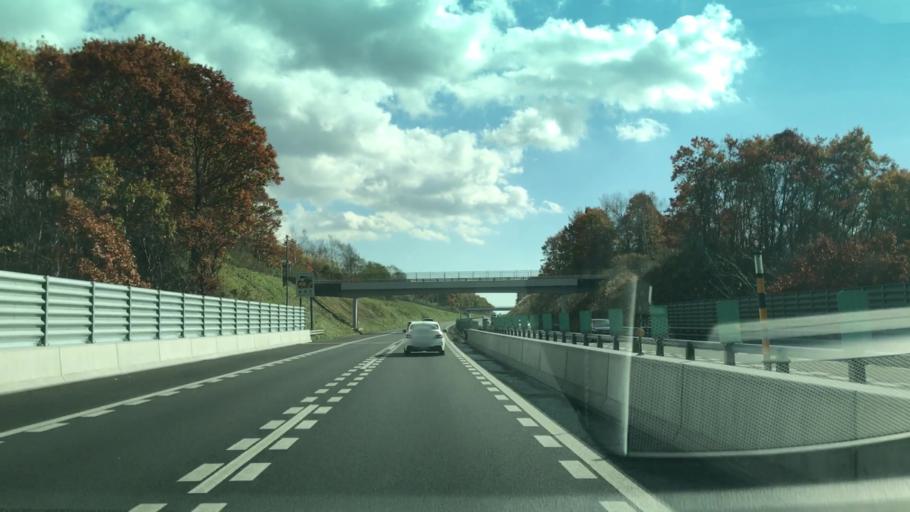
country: JP
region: Hokkaido
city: Kitahiroshima
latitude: 42.9228
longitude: 141.5421
